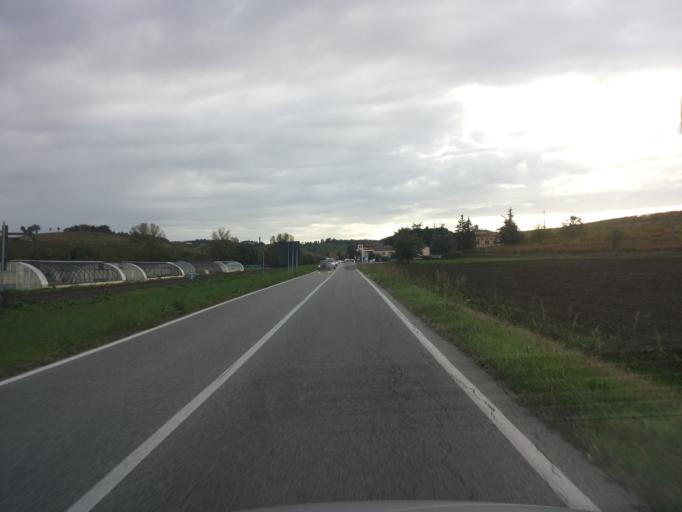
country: IT
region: Piedmont
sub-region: Provincia di Alessandria
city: San Giorgio Monferrato
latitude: 45.1095
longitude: 8.4398
